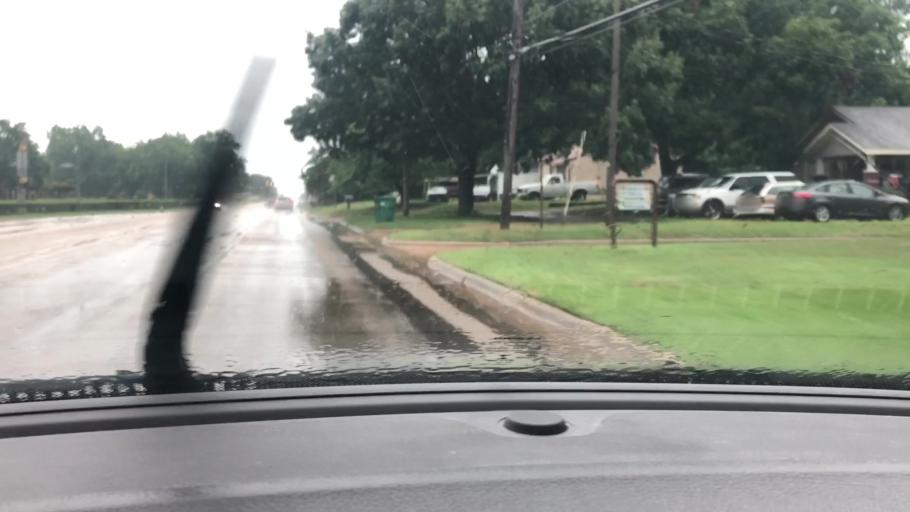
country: US
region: Texas
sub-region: Bowie County
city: Wake Village
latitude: 33.4440
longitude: -94.0804
